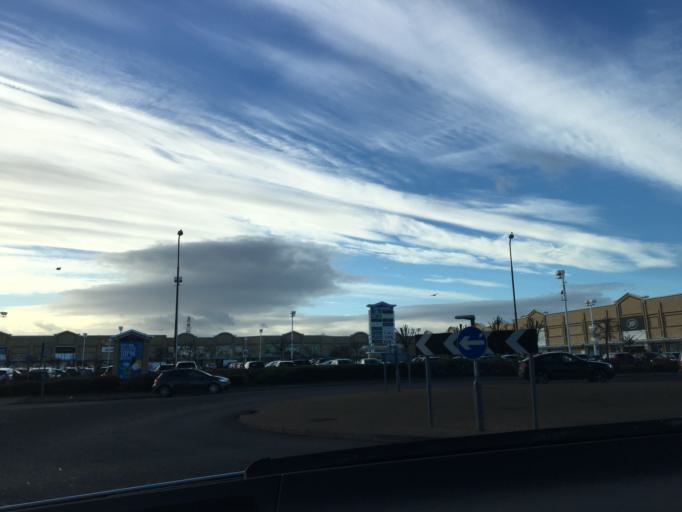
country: GB
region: Scotland
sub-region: Midlothian
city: Dalkeith
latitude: 55.9329
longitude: -3.1054
